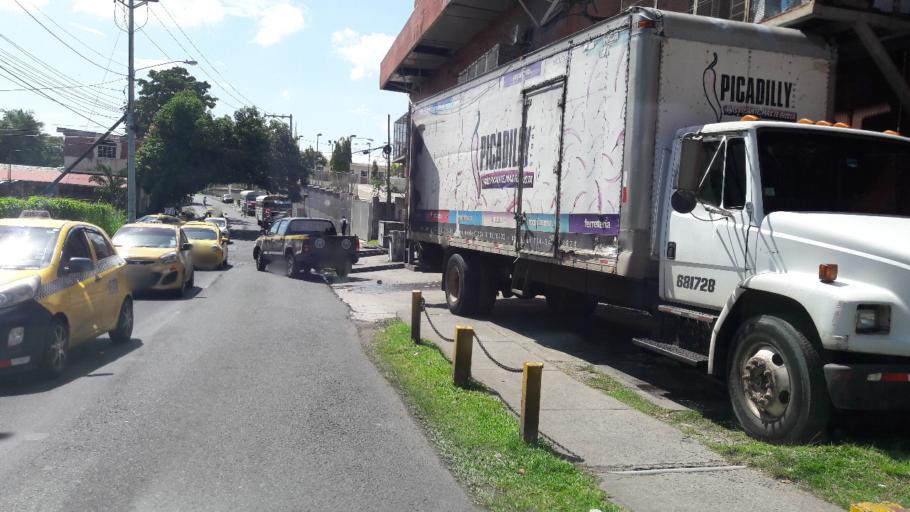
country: PA
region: Panama
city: San Miguelito
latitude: 9.0481
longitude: -79.5055
